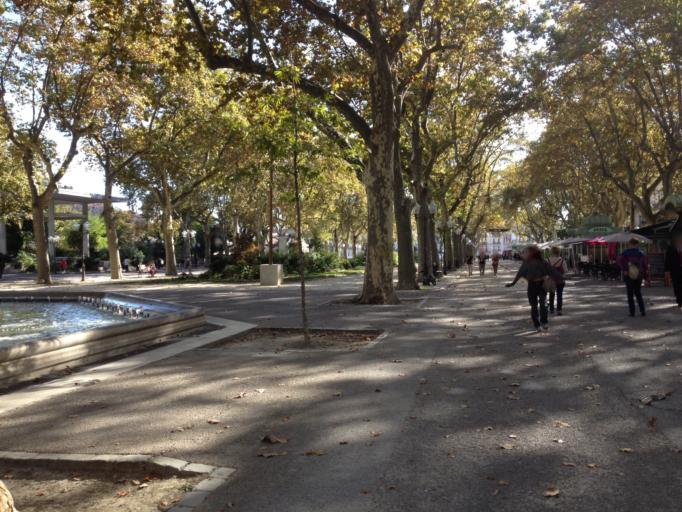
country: FR
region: Languedoc-Roussillon
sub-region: Departement de l'Herault
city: Montpellier
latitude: 43.6115
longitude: 3.8811
